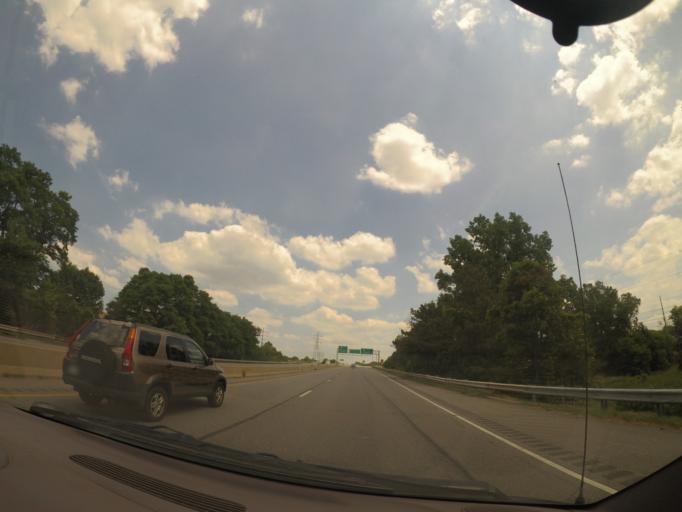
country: US
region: Indiana
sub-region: Saint Joseph County
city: Gulivoire Park
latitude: 41.6247
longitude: -86.2587
